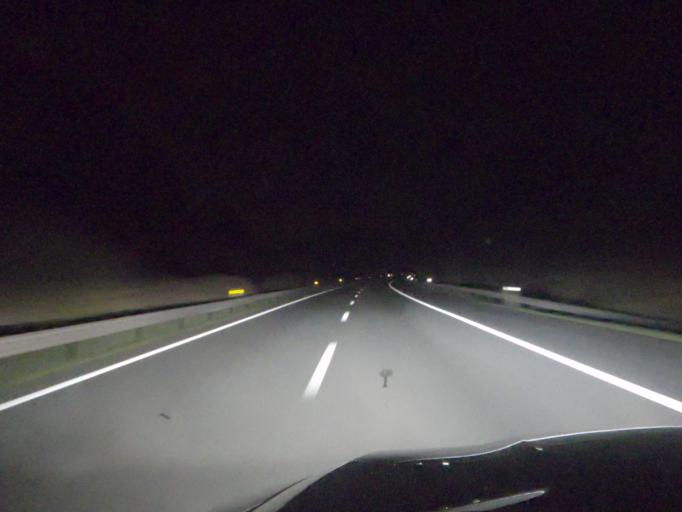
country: PT
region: Aveiro
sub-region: Aveiro
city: Eixo
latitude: 40.6404
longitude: -8.5238
